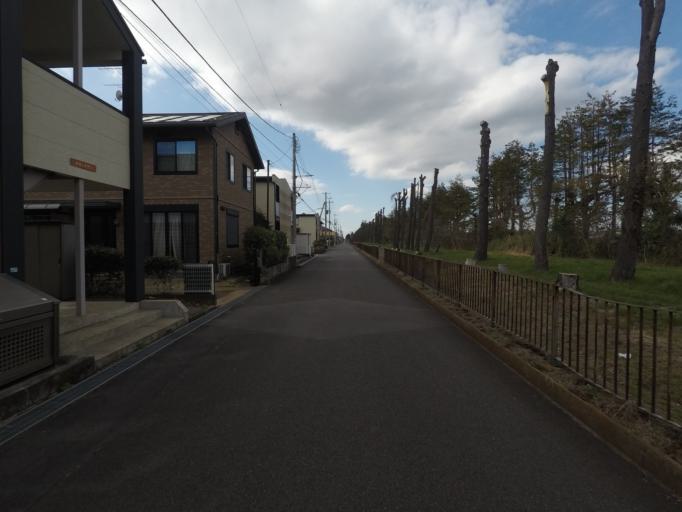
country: JP
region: Ibaraki
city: Ushiku
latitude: 36.0222
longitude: 140.1043
